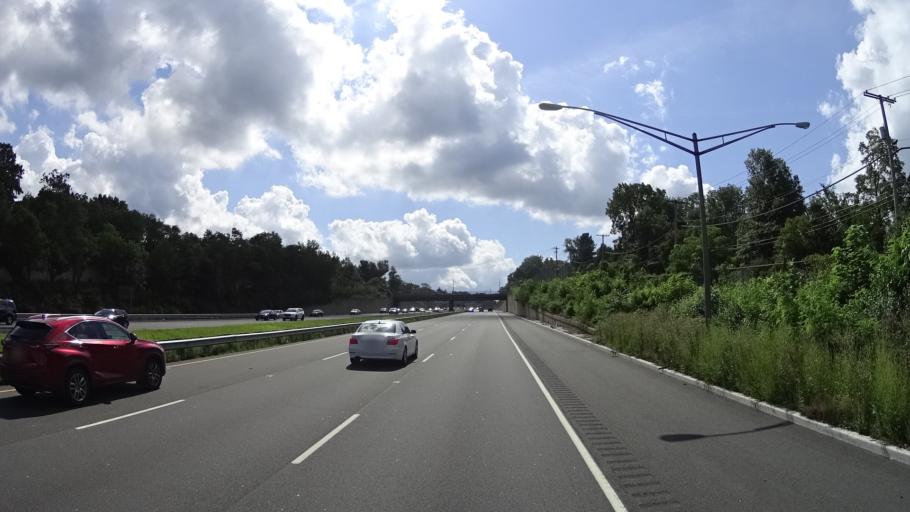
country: US
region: New Jersey
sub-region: Union County
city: Summit
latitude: 40.7346
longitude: -74.3564
